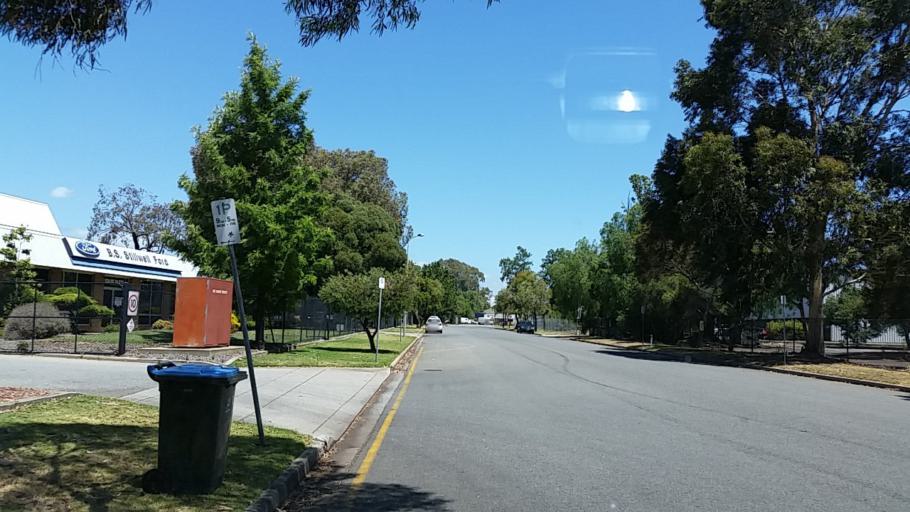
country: AU
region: South Australia
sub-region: Prospect
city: Prospect
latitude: -34.8684
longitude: 138.5733
